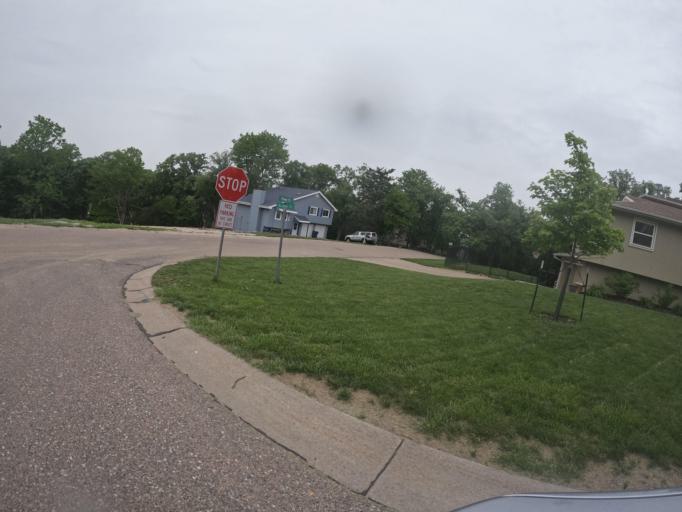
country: US
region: Nebraska
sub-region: Sarpy County
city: Offutt Air Force Base
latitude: 41.0520
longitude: -95.9695
